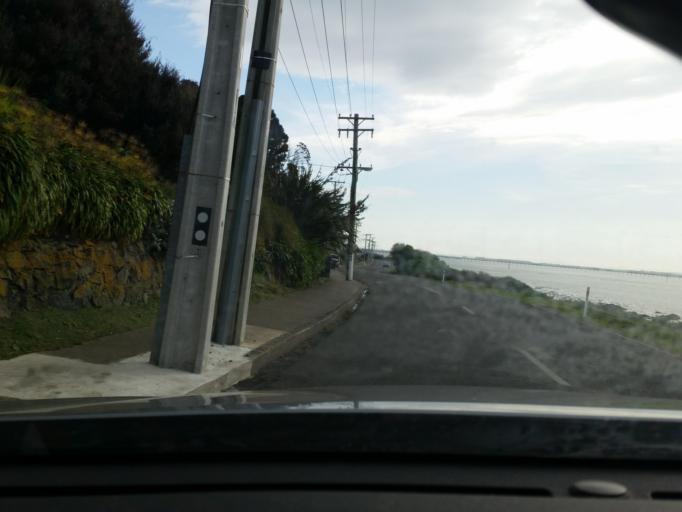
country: NZ
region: Southland
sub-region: Invercargill City
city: Bluff
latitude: -46.6090
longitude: 168.3567
